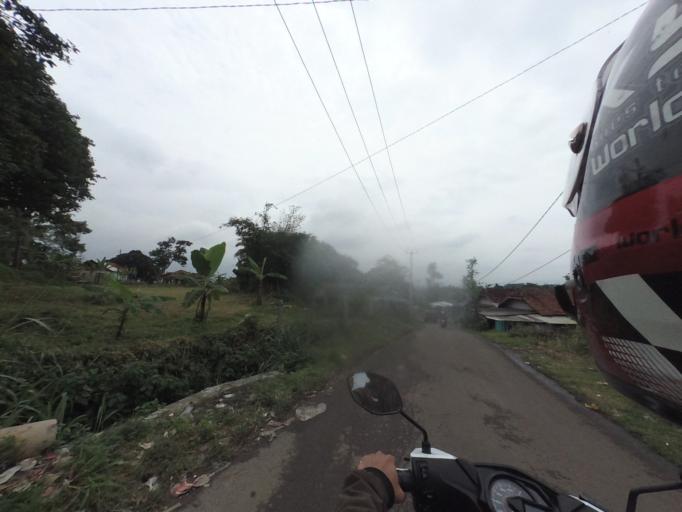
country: ID
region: West Java
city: Bogor
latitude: -6.6159
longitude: 106.7490
